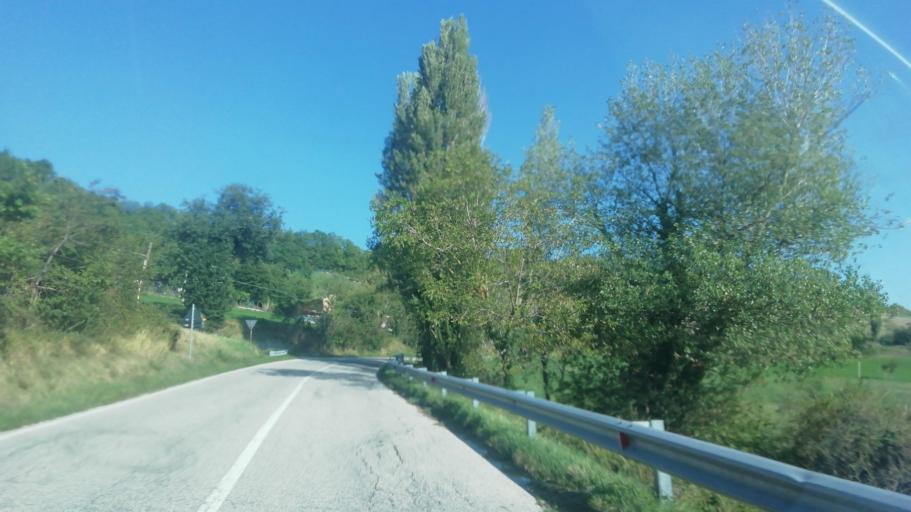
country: IT
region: The Marches
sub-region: Provincia di Pesaro e Urbino
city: Frontone
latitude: 43.5431
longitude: 12.7271
